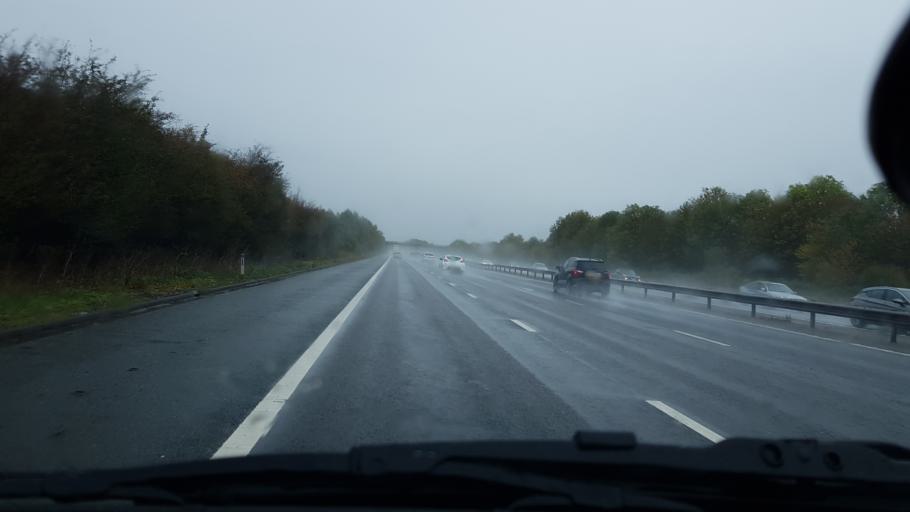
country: GB
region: England
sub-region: Worcestershire
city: Bredon
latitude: 52.0082
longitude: -2.1218
